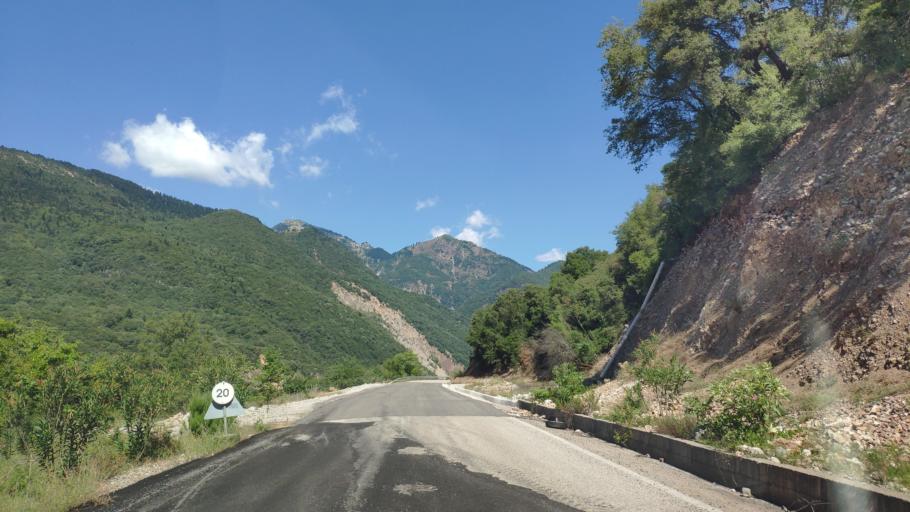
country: GR
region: Central Greece
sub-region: Nomos Evrytanias
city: Kerasochori
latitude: 39.0248
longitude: 21.6018
